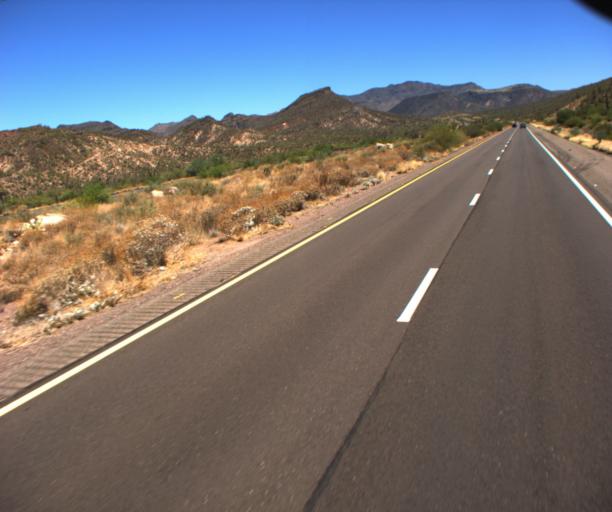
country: US
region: Arizona
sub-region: Maricopa County
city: Rio Verde
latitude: 33.7656
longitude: -111.4939
